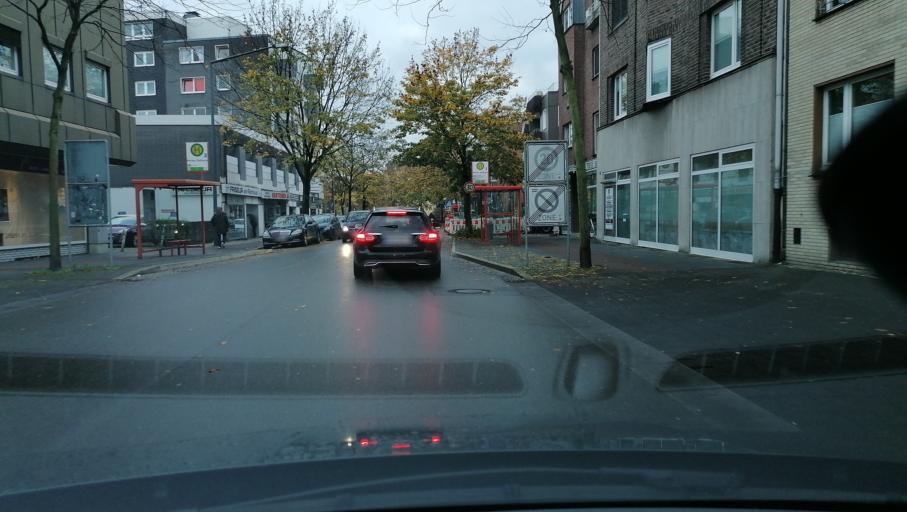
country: DE
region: North Rhine-Westphalia
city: Herten
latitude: 51.5936
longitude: 7.1359
